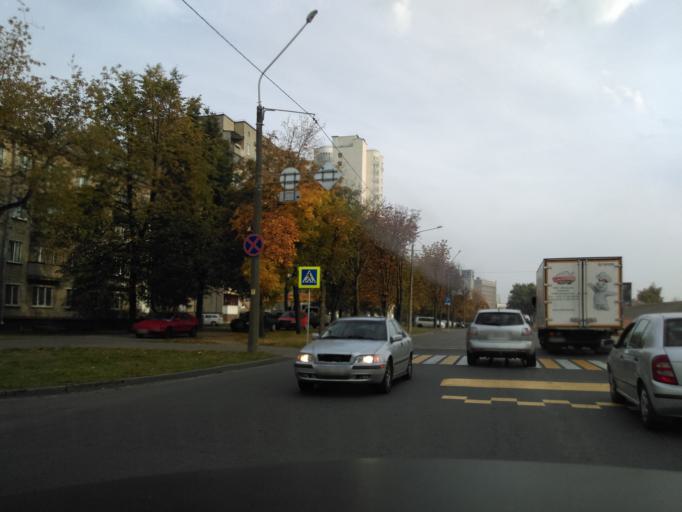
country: BY
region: Minsk
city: Minsk
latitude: 53.9075
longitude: 27.5923
